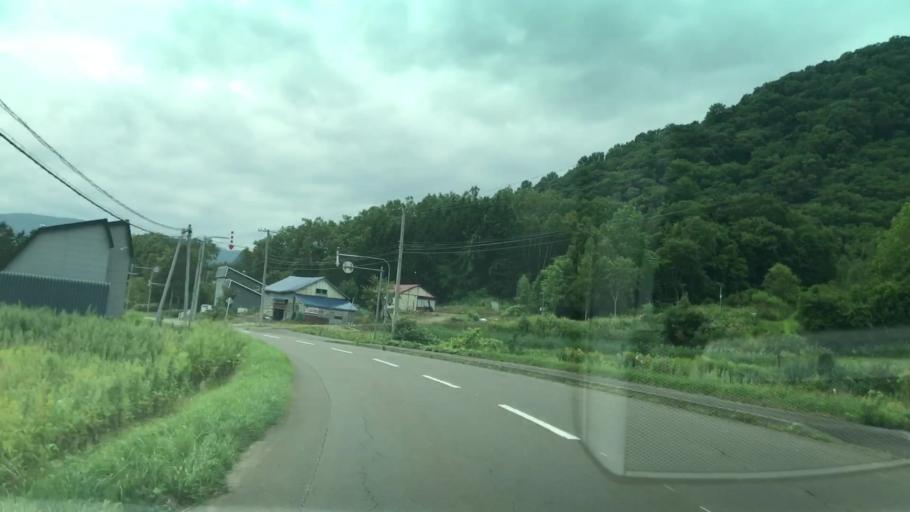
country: JP
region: Hokkaido
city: Yoichi
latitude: 43.0730
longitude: 140.8164
